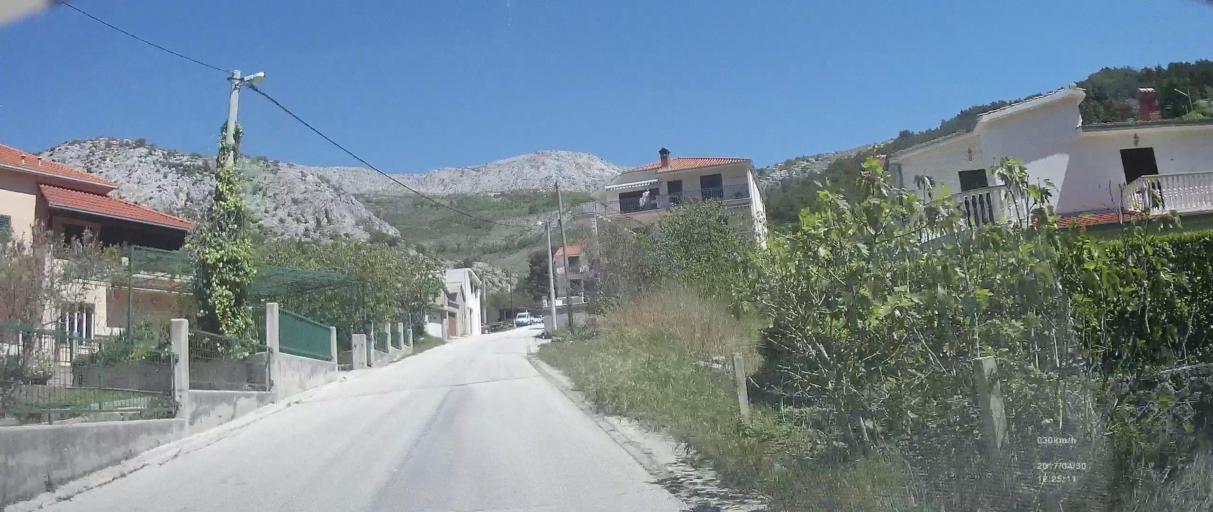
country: HR
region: Splitsko-Dalmatinska
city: Srinjine
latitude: 43.5092
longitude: 16.5905
